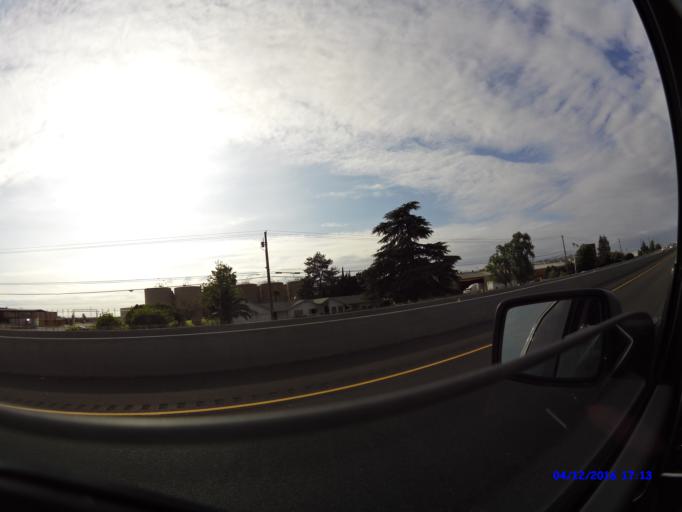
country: US
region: California
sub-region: San Joaquin County
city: Manteca
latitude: 37.8533
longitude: -121.2184
